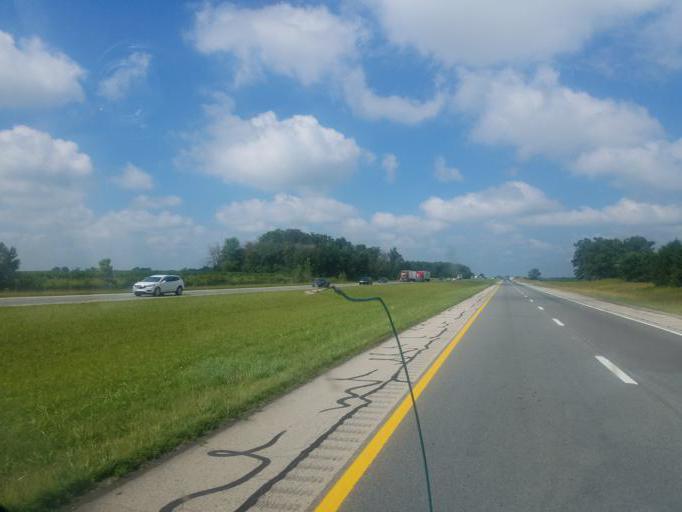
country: US
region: Ohio
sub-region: Madison County
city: Bethel
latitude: 39.7098
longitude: -83.4228
